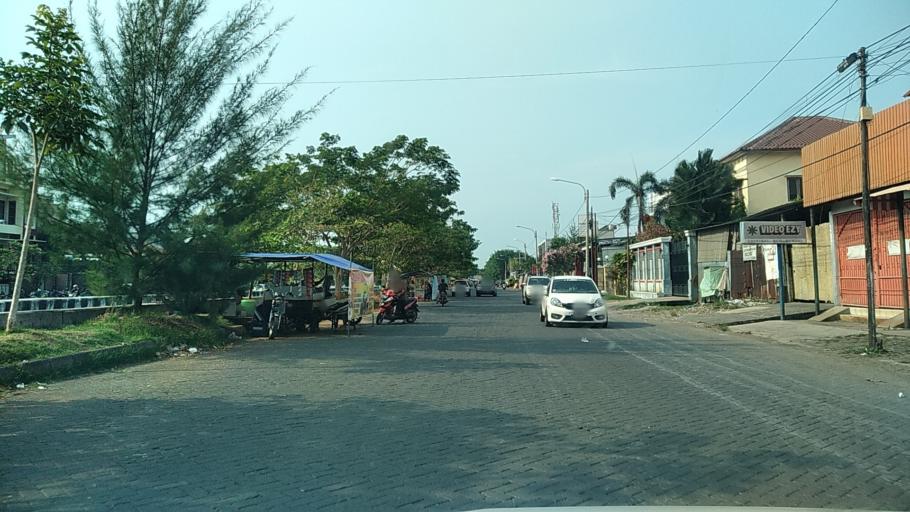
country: ID
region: Central Java
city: Semarang
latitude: -6.9618
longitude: 110.4108
